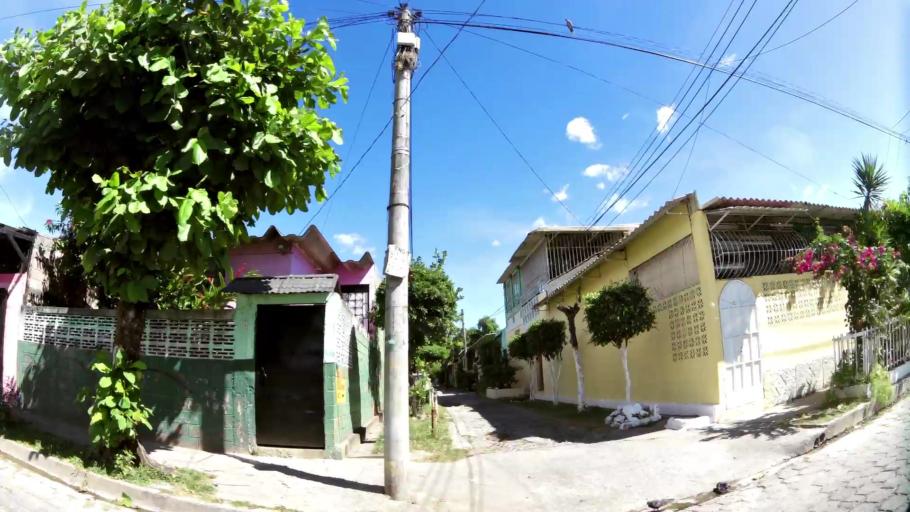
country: SV
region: San Salvador
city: Apopa
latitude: 13.8089
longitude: -89.1814
